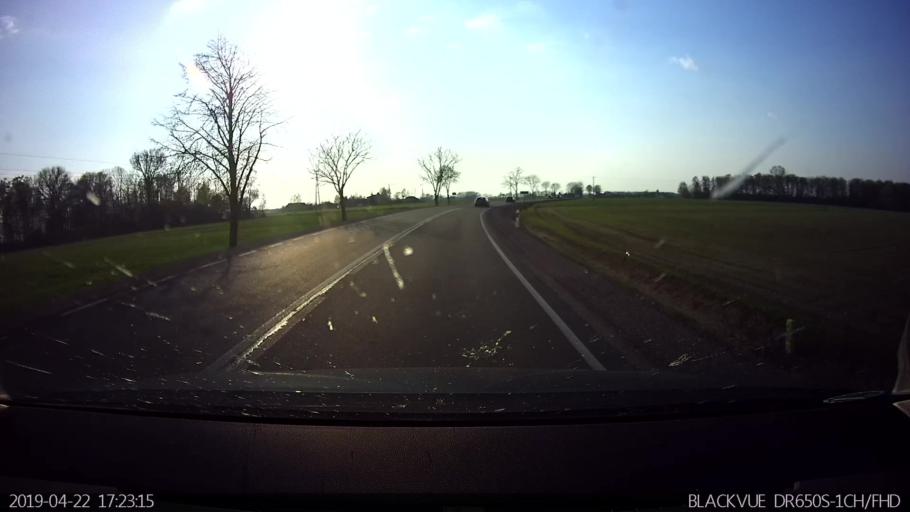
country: PL
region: Masovian Voivodeship
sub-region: Powiat sokolowski
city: Repki
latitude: 52.3900
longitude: 22.3212
